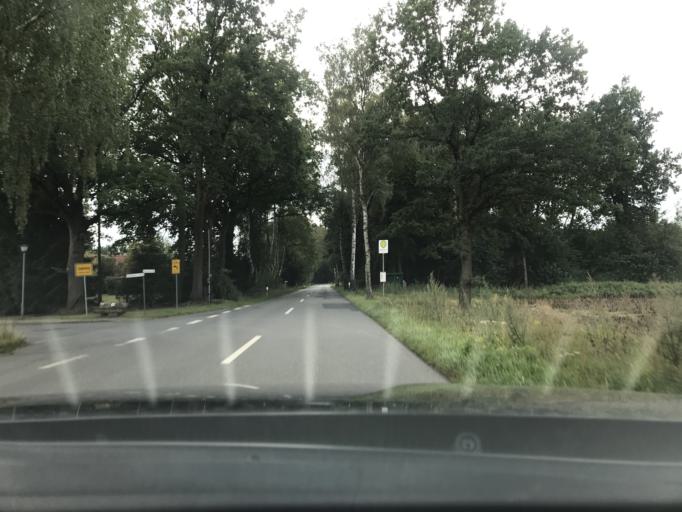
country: DE
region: Lower Saxony
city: Suderburg
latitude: 52.8885
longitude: 10.4423
